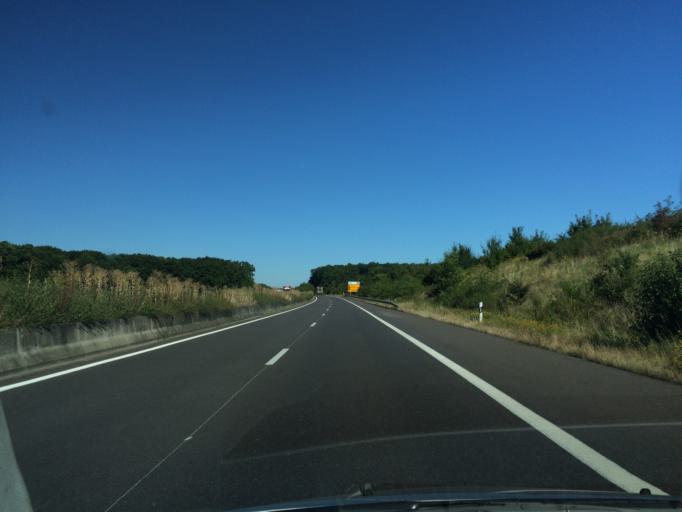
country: LU
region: Grevenmacher
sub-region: Canton de Remich
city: Mondorf-les-Bains
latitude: 49.5046
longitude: 6.3043
